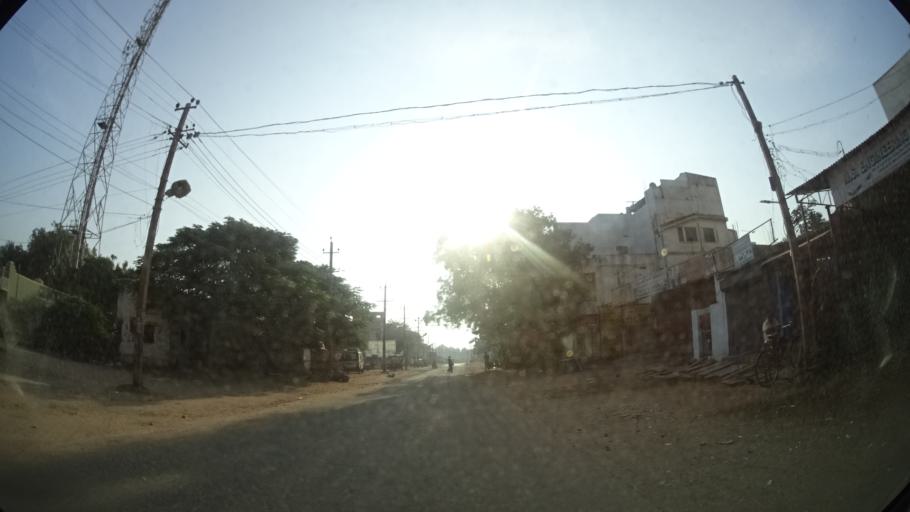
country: IN
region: Karnataka
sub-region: Bellary
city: Hospet
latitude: 15.2655
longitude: 76.4012
